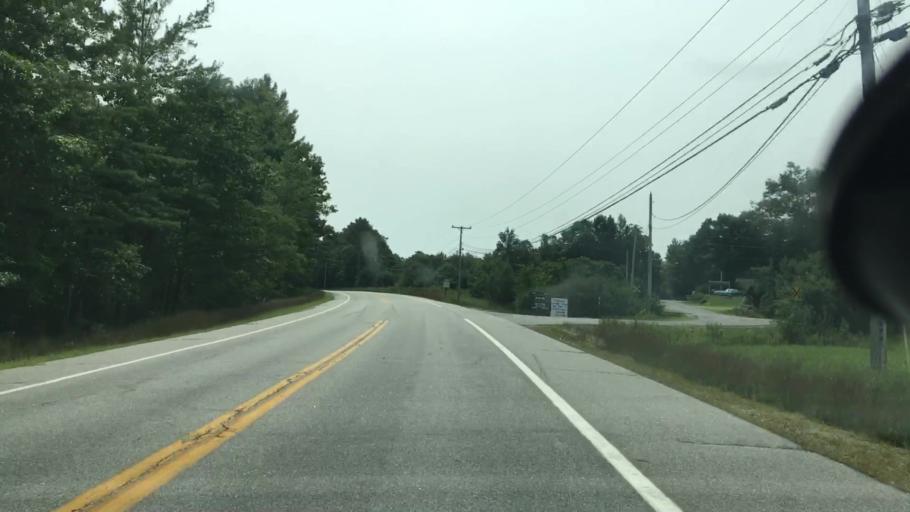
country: US
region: Maine
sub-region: Androscoggin County
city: Livermore Falls
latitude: 44.4168
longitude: -70.1452
